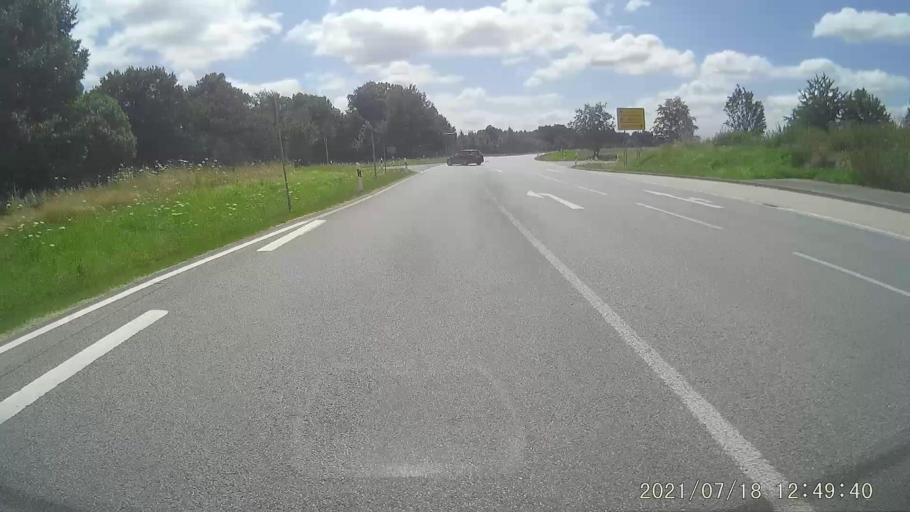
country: DE
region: Saxony
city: Reichenbach
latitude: 51.2004
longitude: 14.7600
